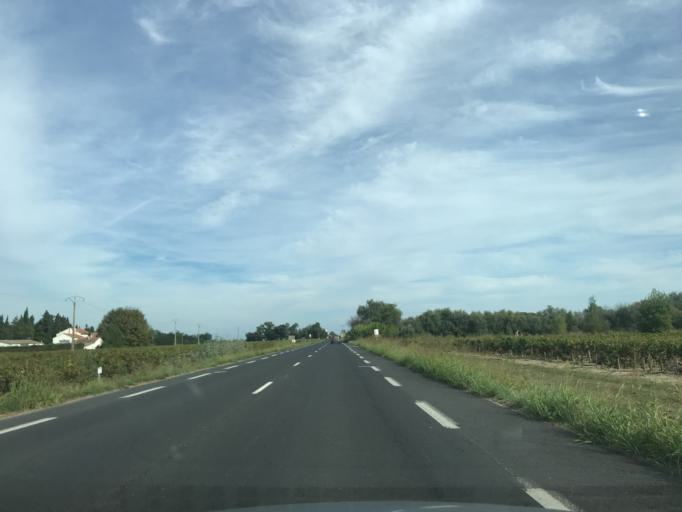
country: FR
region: Languedoc-Roussillon
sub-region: Departement du Gard
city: Aigues-Mortes
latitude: 43.5763
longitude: 4.2941
